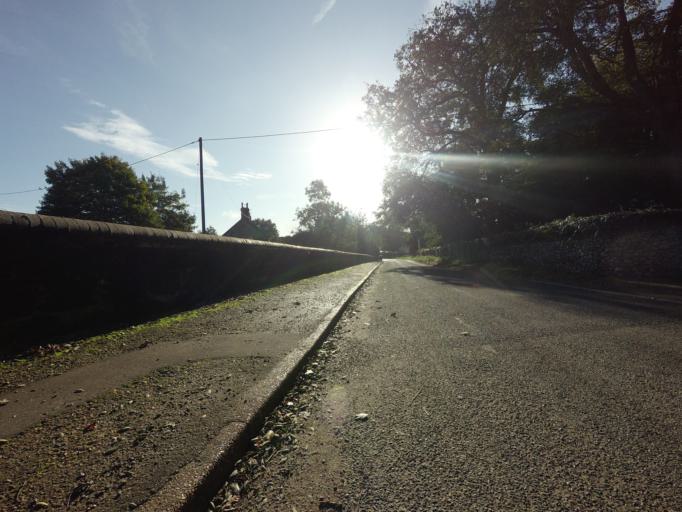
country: GB
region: England
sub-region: Norfolk
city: Dersingham
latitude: 52.8345
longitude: 0.5844
